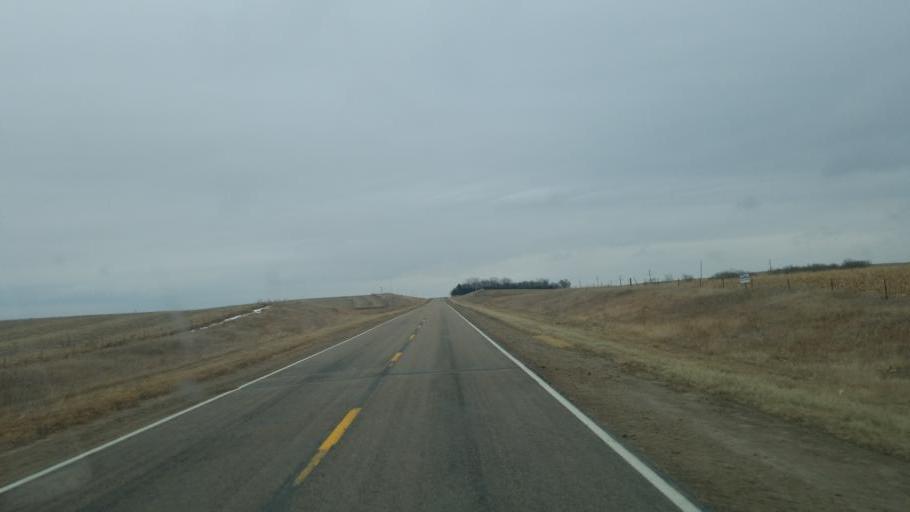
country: US
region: Nebraska
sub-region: Knox County
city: Bloomfield
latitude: 42.5978
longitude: -97.5787
